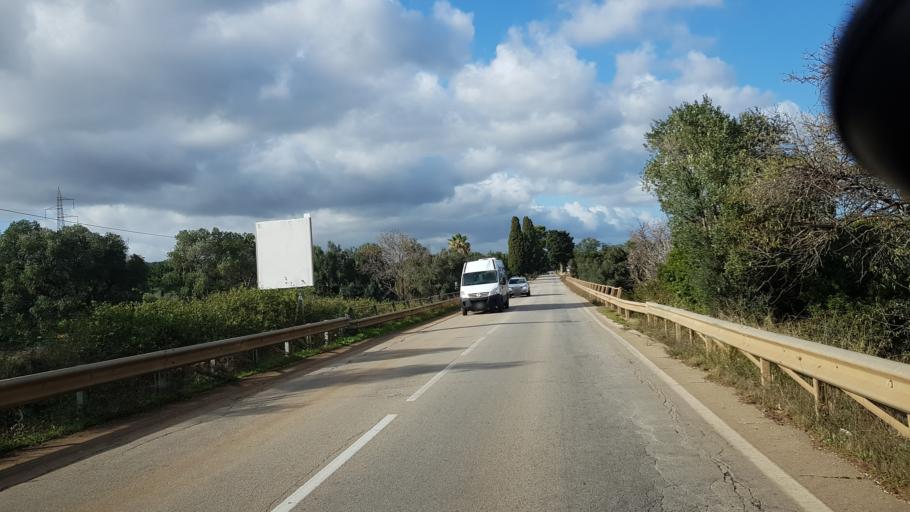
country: IT
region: Apulia
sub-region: Provincia di Brindisi
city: Ostuni
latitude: 40.7536
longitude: 17.5442
